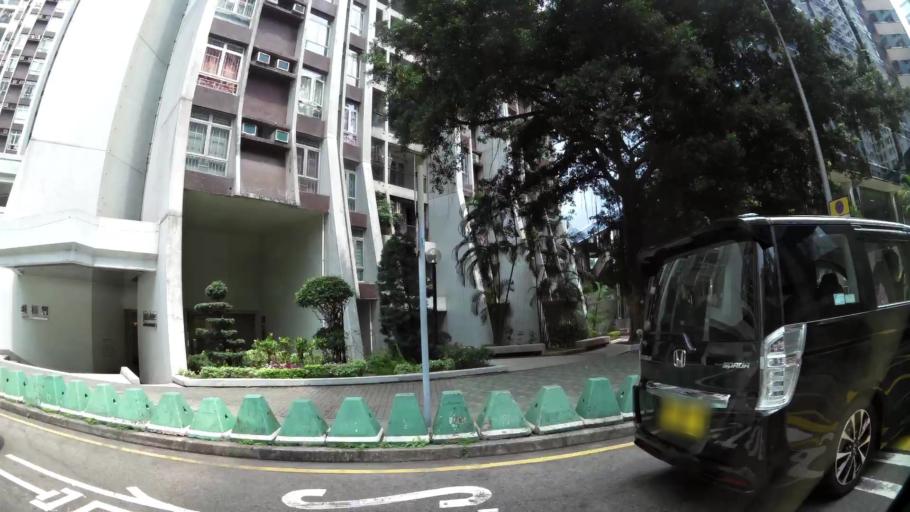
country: HK
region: Wanchai
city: Wan Chai
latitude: 22.2872
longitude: 114.2166
